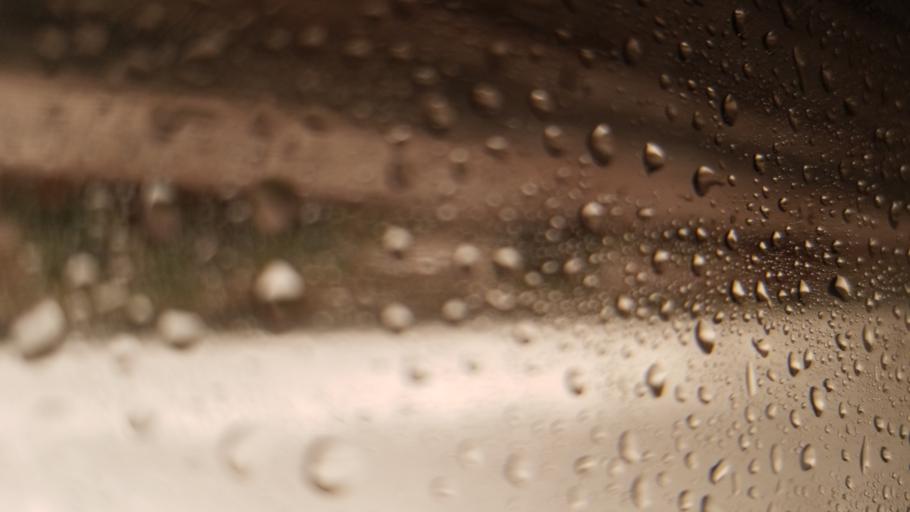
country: US
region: Arizona
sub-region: Navajo County
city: Joseph City
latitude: 34.9434
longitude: -110.3212
